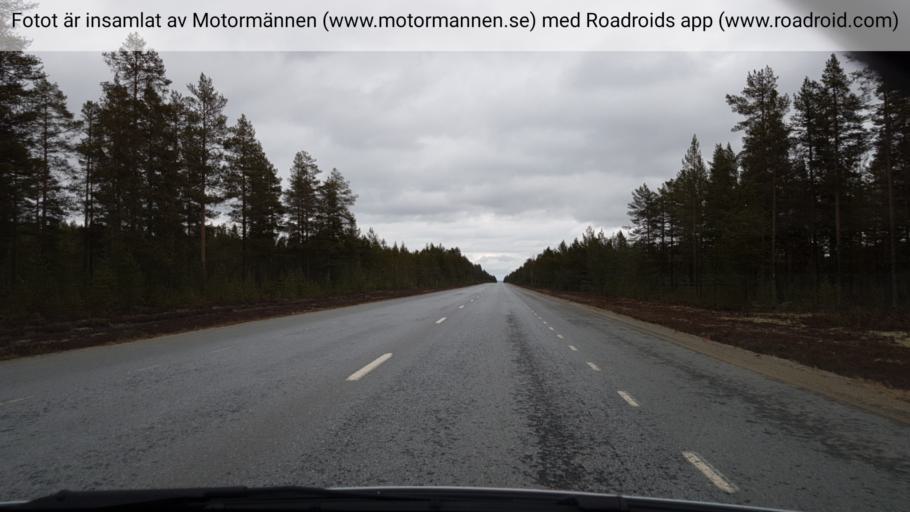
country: SE
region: Vaesterbotten
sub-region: Bjurholms Kommun
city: Bjurholm
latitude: 63.9339
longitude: 18.9598
